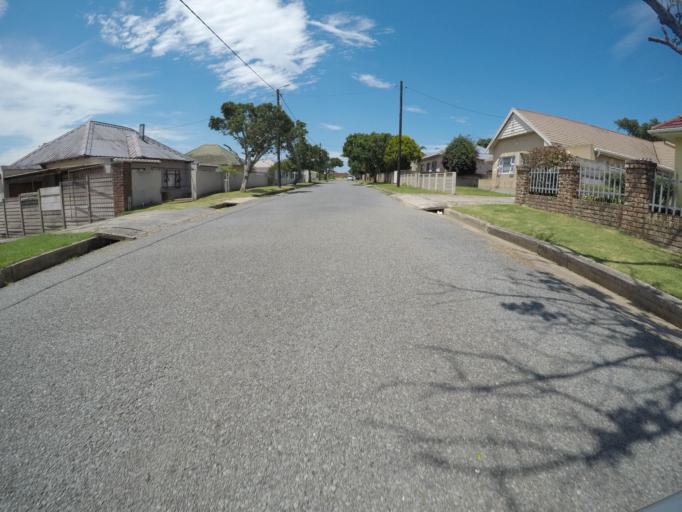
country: ZA
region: Eastern Cape
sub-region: Buffalo City Metropolitan Municipality
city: East London
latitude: -33.0331
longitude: 27.8619
